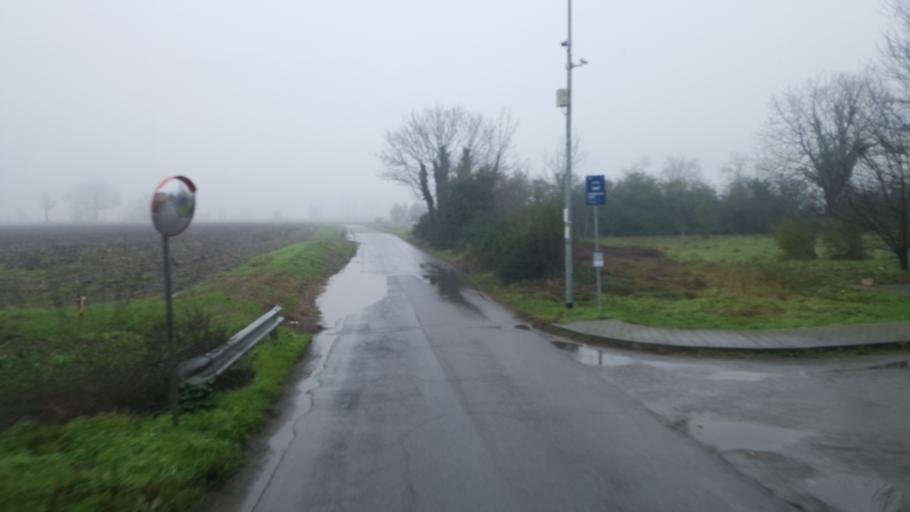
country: IT
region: Lombardy
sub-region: Provincia di Pavia
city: Torrevecchia Pia
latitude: 45.2805
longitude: 9.2804
